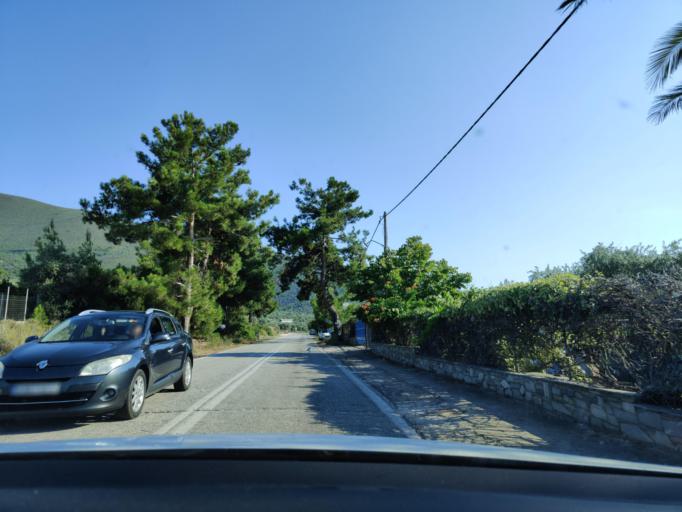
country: GR
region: East Macedonia and Thrace
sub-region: Nomos Kavalas
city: Prinos
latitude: 40.6900
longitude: 24.5266
